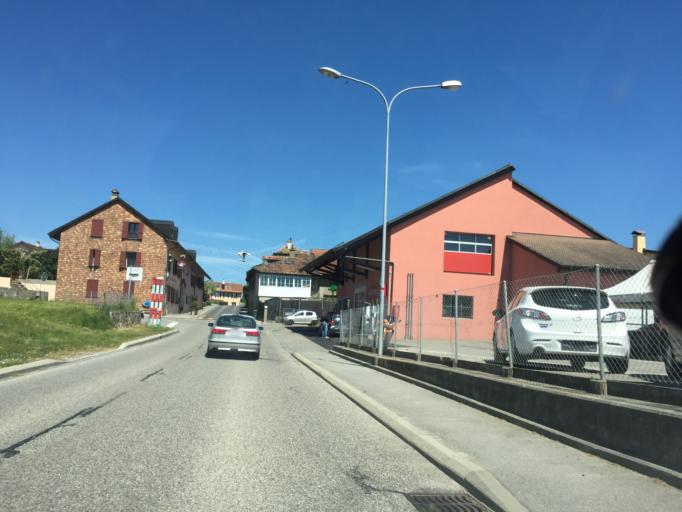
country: CH
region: Vaud
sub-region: Morges District
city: Apples
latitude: 46.5286
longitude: 6.4414
